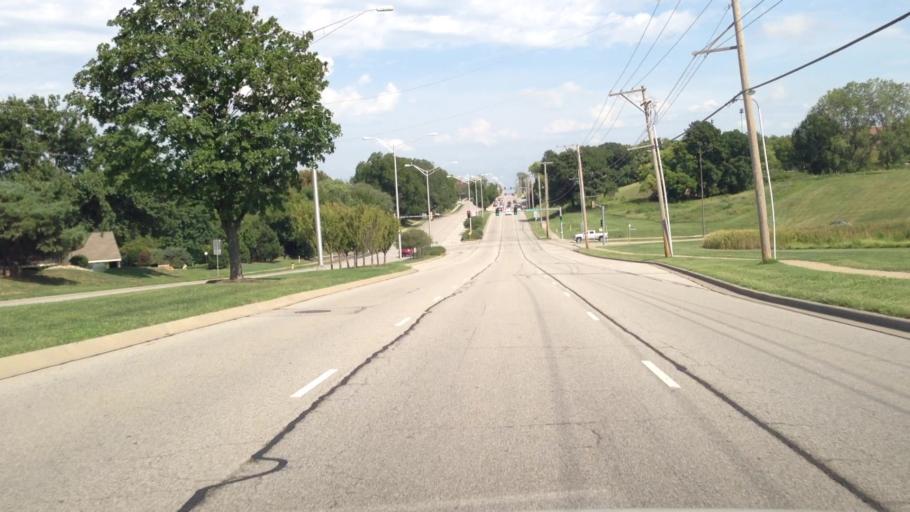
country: US
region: Kansas
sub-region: Johnson County
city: Lenexa
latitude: 38.9273
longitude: -94.7357
